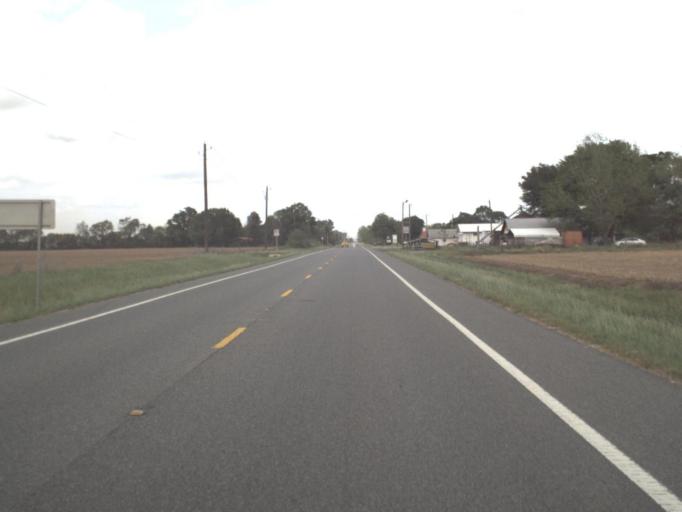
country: US
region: Florida
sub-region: Santa Rosa County
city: Point Baker
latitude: 30.7804
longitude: -87.0926
